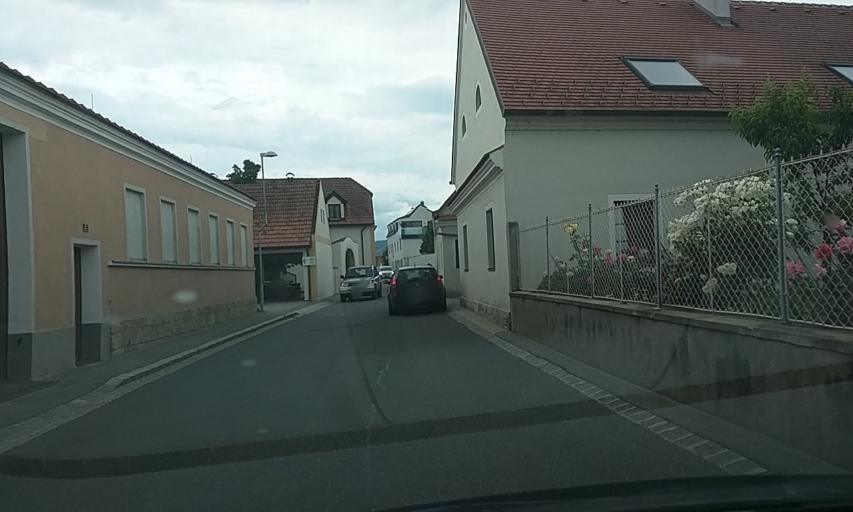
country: AT
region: Lower Austria
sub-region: Politischer Bezirk Krems
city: Weinzierl bei Krems
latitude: 48.3849
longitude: 15.6121
